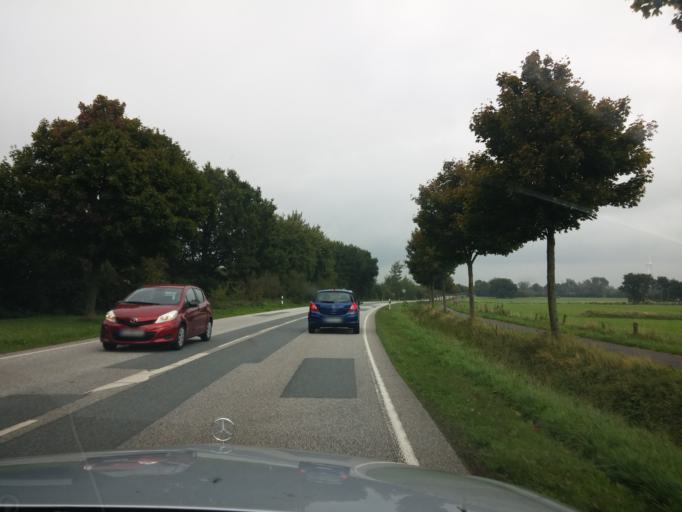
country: DE
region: Schleswig-Holstein
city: Schwesing
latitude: 54.5005
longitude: 9.1416
